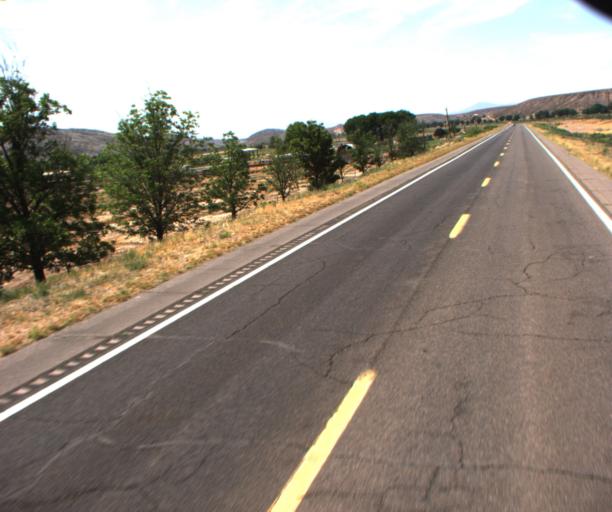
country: US
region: Arizona
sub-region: Greenlee County
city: Clifton
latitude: 32.8506
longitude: -109.1817
